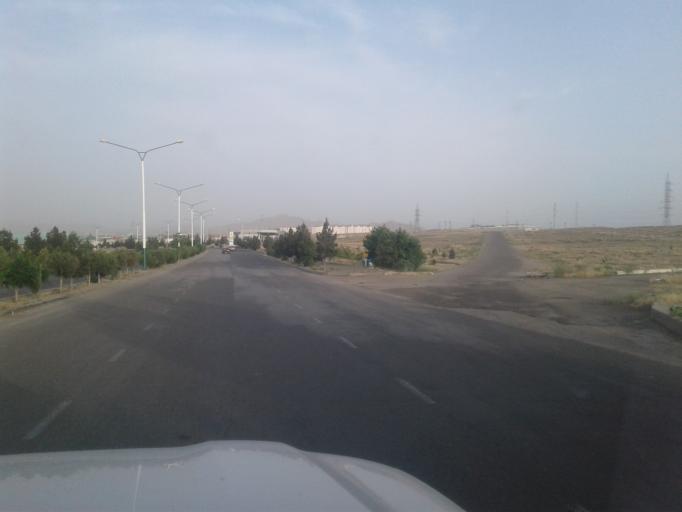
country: TM
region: Balkan
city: Turkmenbasy
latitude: 40.0403
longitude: 52.9742
